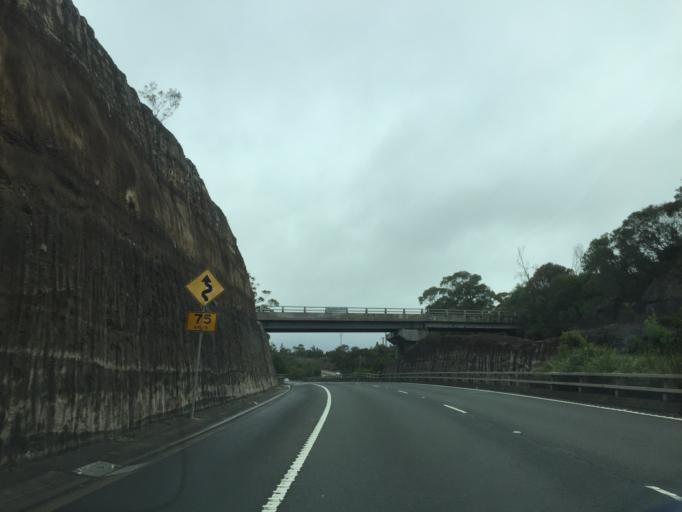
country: AU
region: New South Wales
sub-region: Blue Mountains Municipality
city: Hazelbrook
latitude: -33.7174
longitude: 150.4969
